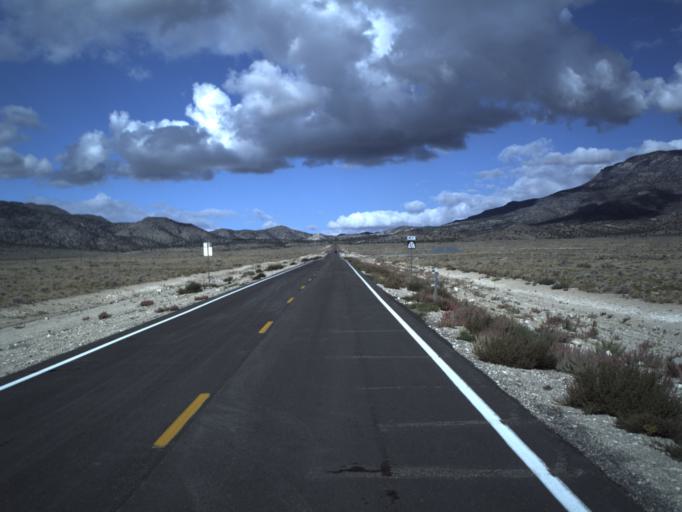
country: US
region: Utah
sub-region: Beaver County
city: Milford
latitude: 38.4918
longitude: -113.4725
